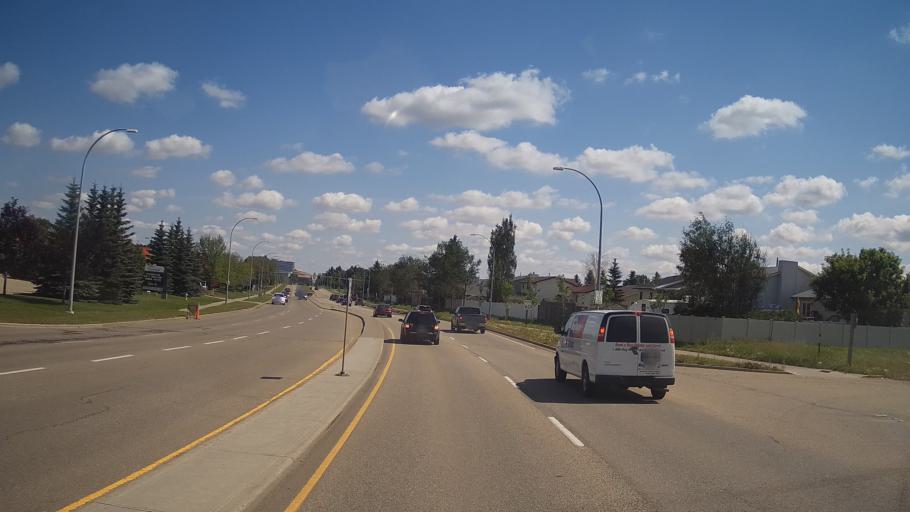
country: CA
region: Alberta
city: St. Albert
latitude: 53.5213
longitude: -113.6528
